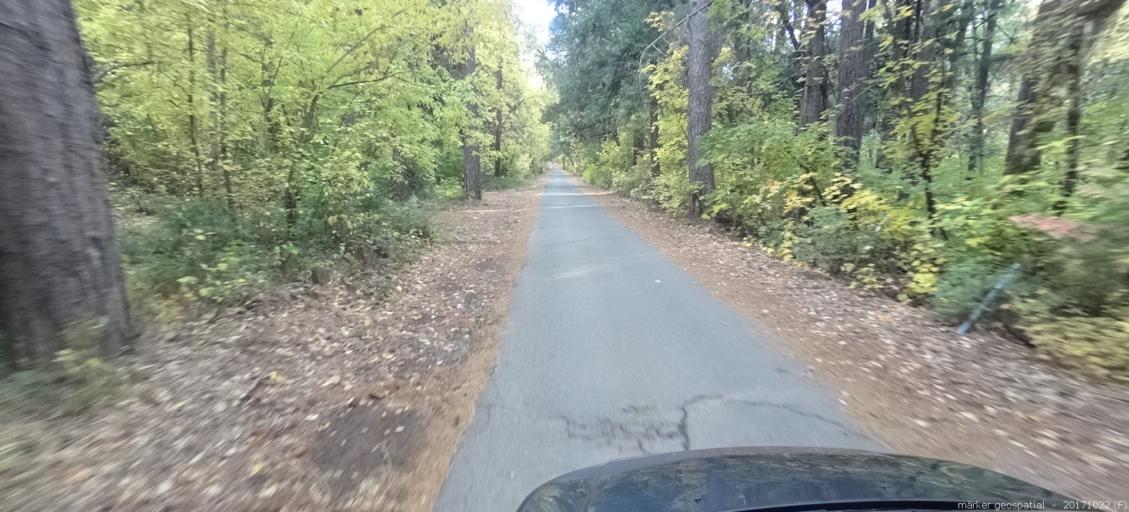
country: US
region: California
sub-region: Siskiyou County
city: Dunsmuir
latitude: 41.1712
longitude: -122.2751
